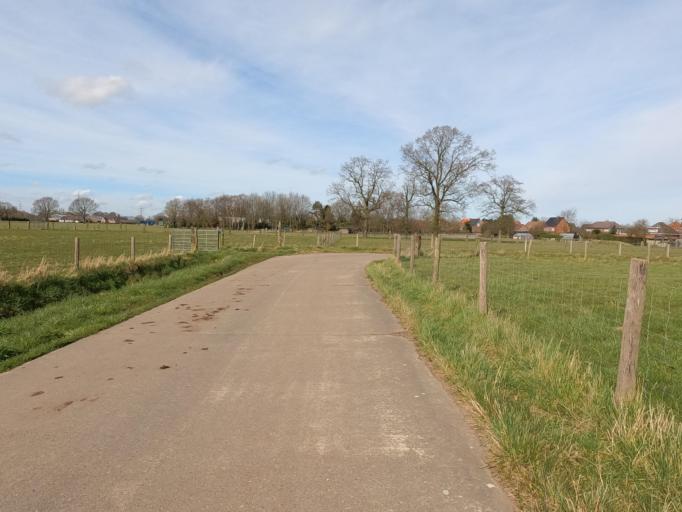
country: BE
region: Flanders
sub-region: Provincie Antwerpen
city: Brecht
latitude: 51.3302
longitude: 4.6716
